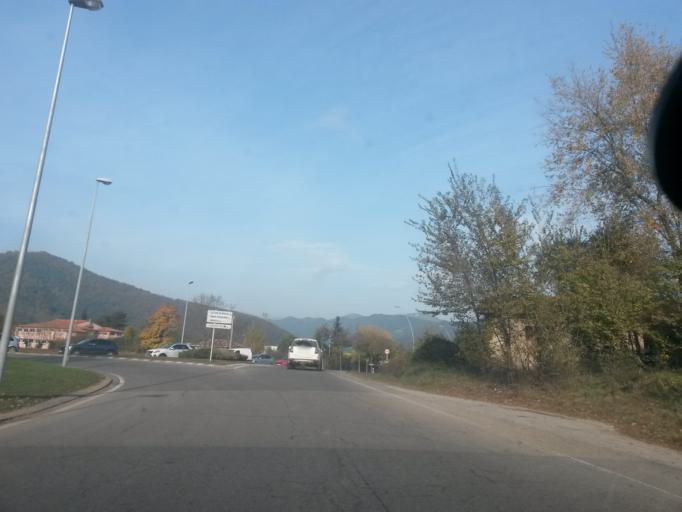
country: ES
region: Catalonia
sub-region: Provincia de Girona
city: MeteOlot
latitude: 42.1968
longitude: 2.4997
